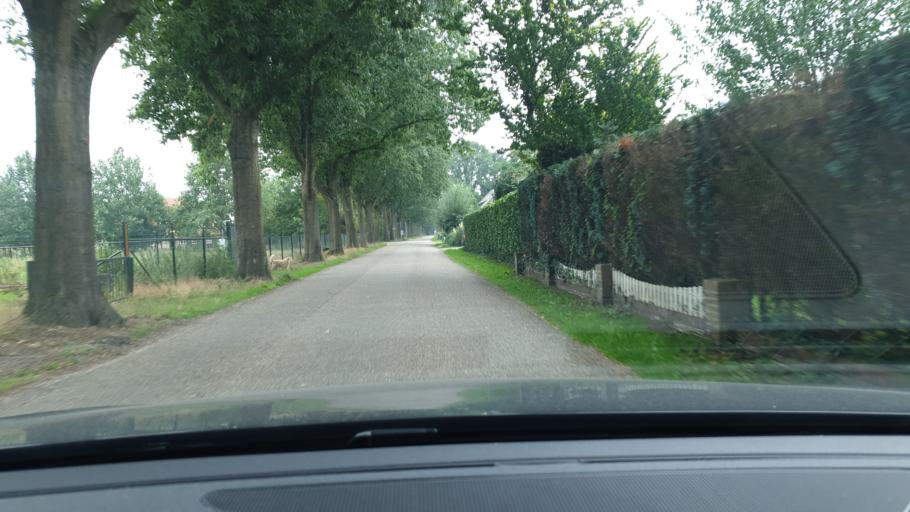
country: NL
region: North Brabant
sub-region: Gemeente Oss
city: Berghem
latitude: 51.7582
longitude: 5.5672
